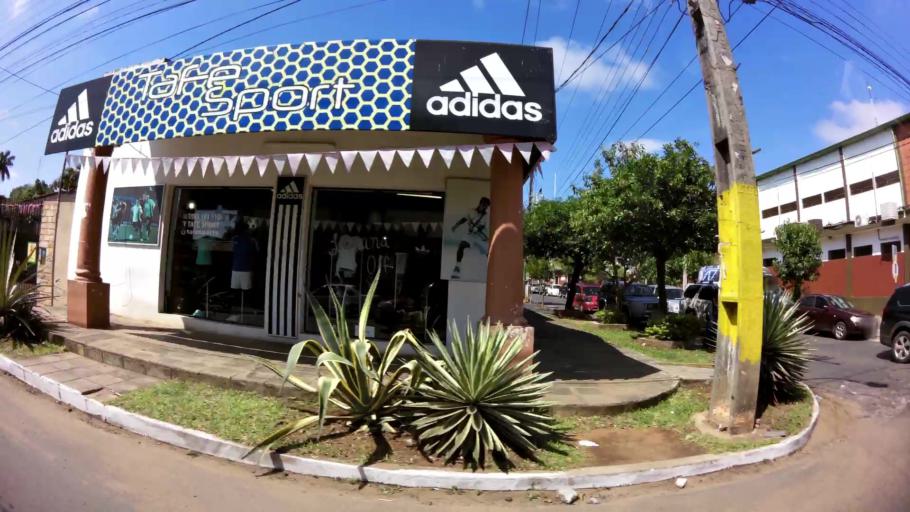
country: PY
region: Central
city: San Lorenzo
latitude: -25.2655
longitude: -57.4903
